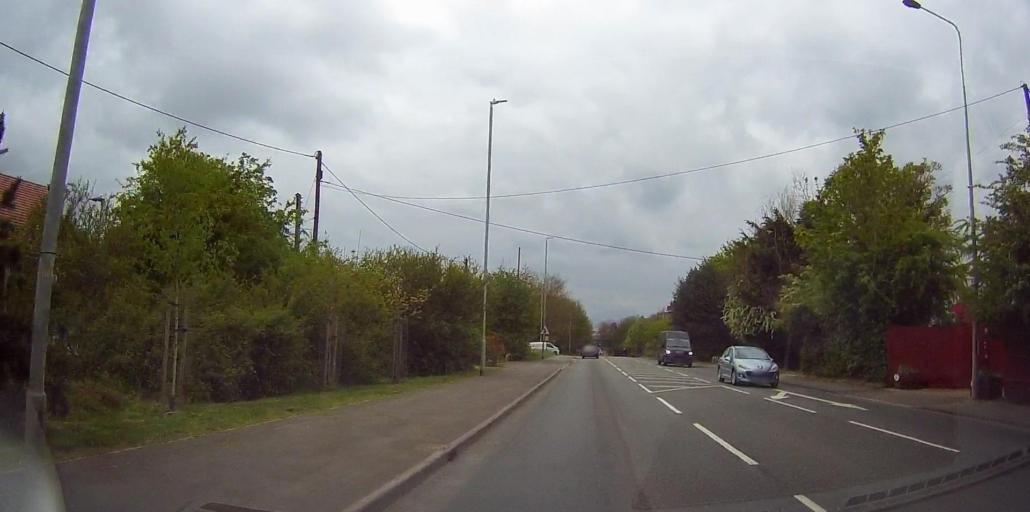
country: GB
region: England
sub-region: Kent
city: Harrietsham
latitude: 51.2421
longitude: 0.6854
